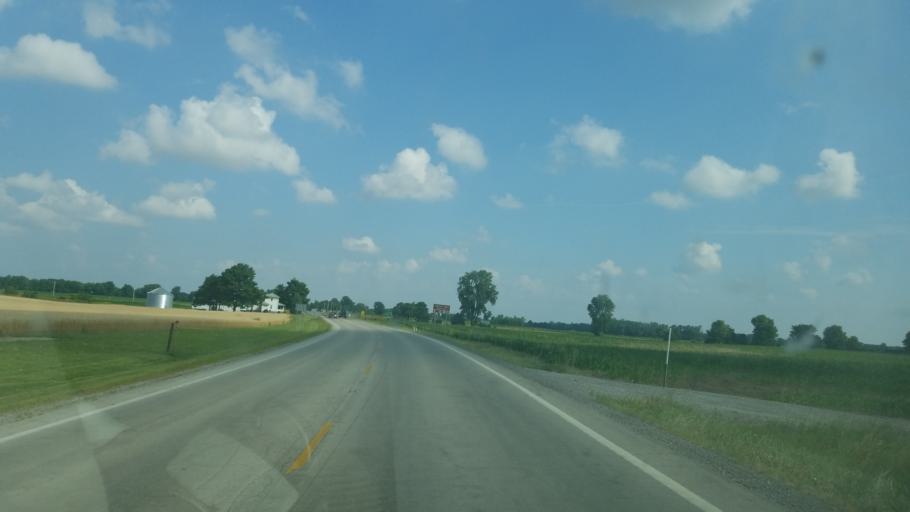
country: US
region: Ohio
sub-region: Logan County
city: Russells Point
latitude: 40.5276
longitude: -83.8296
